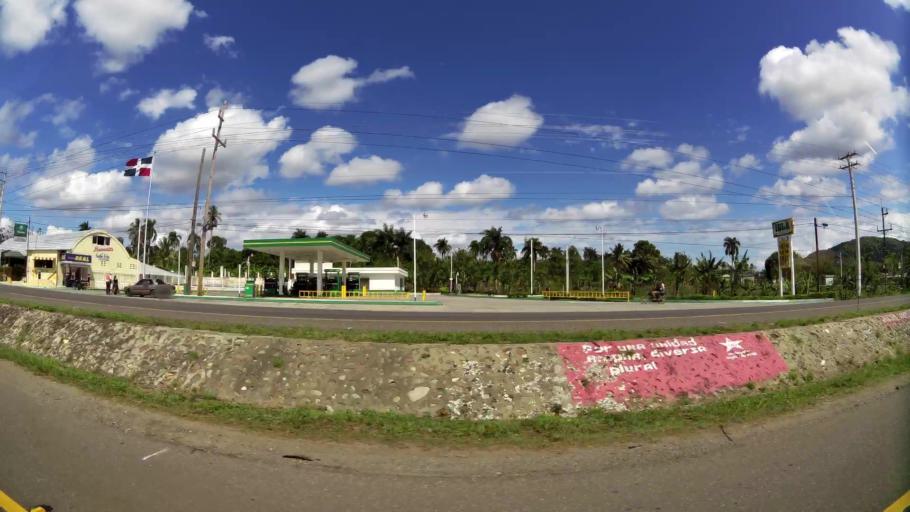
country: DO
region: La Vega
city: Rio Verde Arriba
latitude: 19.3199
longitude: -70.5873
